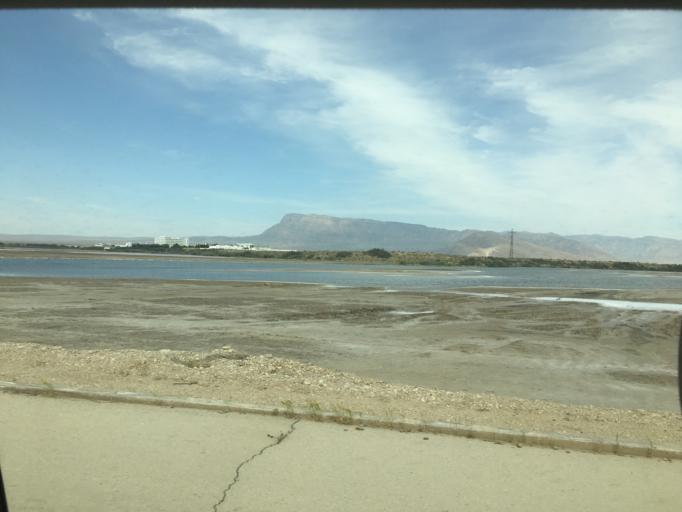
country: TM
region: Balkan
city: Balkanabat
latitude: 39.6203
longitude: 54.1629
